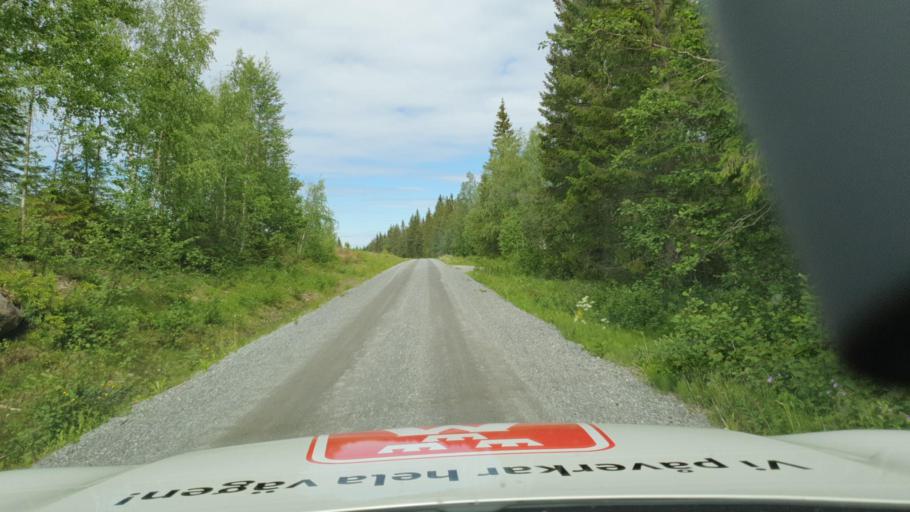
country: SE
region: Vaesterbotten
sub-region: Skelleftea Kommun
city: Langsele
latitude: 64.6229
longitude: 20.2606
